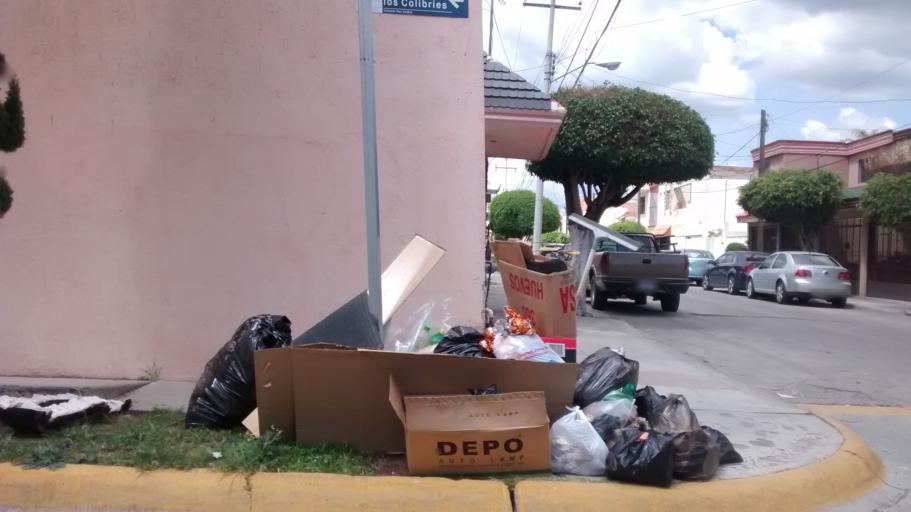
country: MX
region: Guanajuato
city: Leon
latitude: 21.1026
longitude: -101.6476
